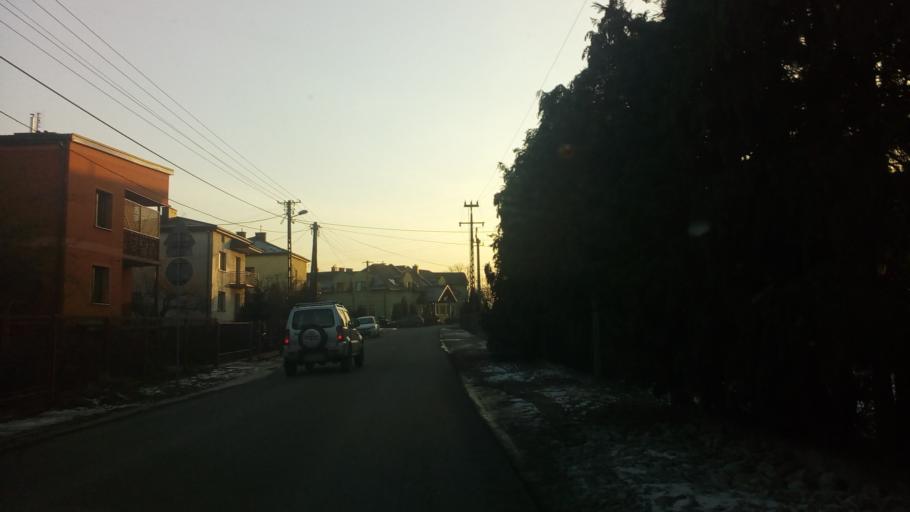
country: PL
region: Lesser Poland Voivodeship
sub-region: Powiat nowosadecki
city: Chelmiec
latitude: 49.6319
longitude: 20.6636
